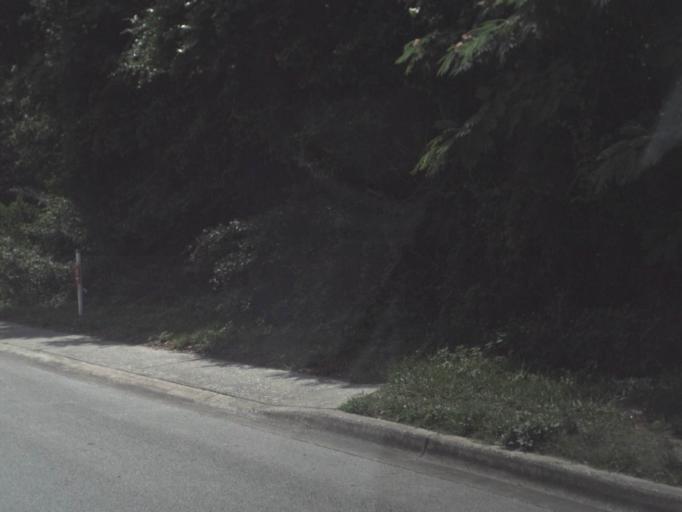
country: US
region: Florida
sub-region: Clay County
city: Bellair-Meadowbrook Terrace
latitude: 30.2913
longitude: -81.7848
